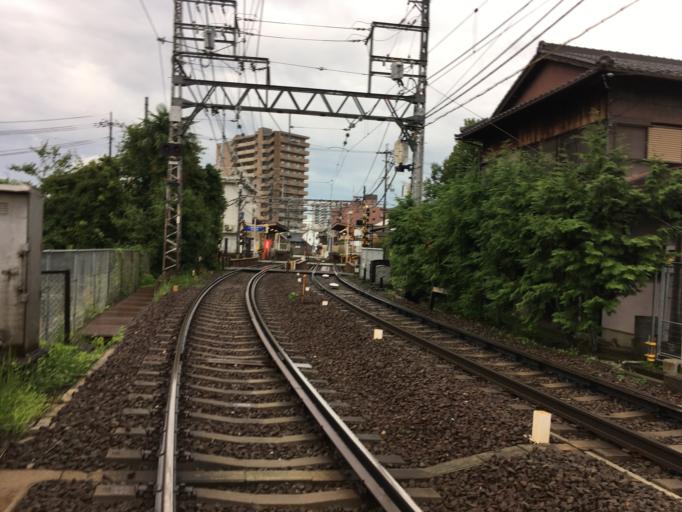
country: JP
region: Shiga Prefecture
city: Otsu-shi
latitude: 35.0136
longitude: 135.8591
